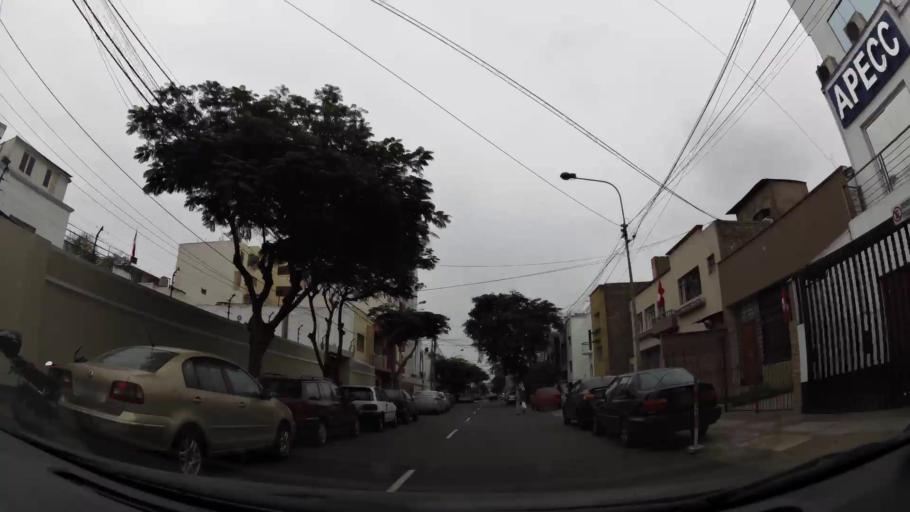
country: PE
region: Lima
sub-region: Lima
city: San Isidro
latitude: -12.0903
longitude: -77.0357
